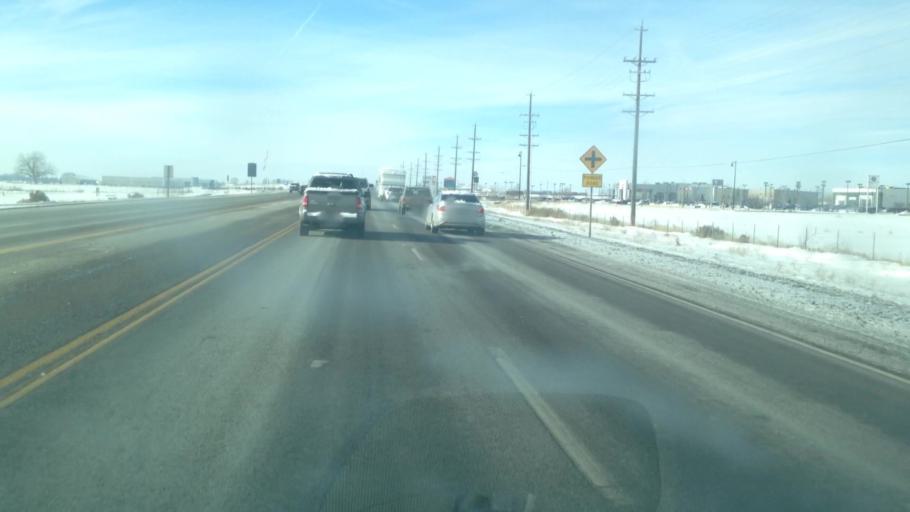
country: US
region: Idaho
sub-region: Bonneville County
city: Idaho Falls
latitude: 43.4678
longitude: -112.0707
